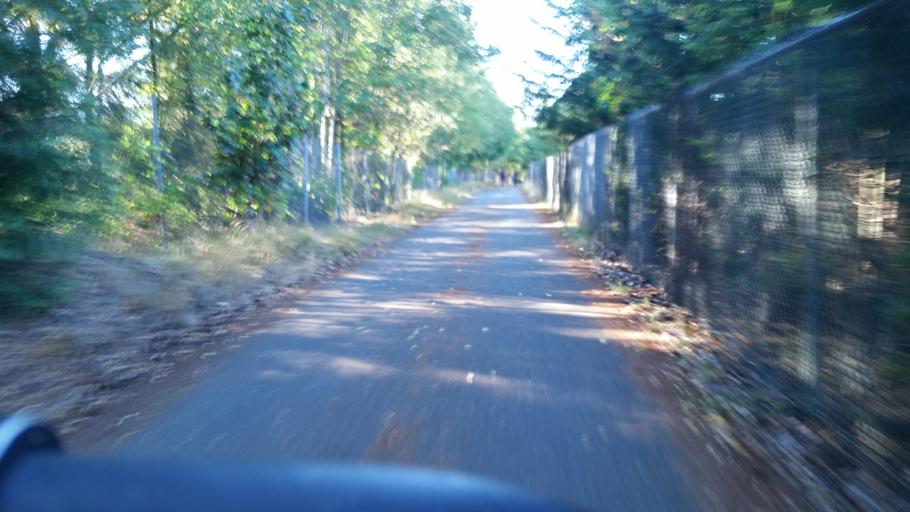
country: US
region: Washington
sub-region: King County
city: Redmond
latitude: 47.6500
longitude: -122.1374
